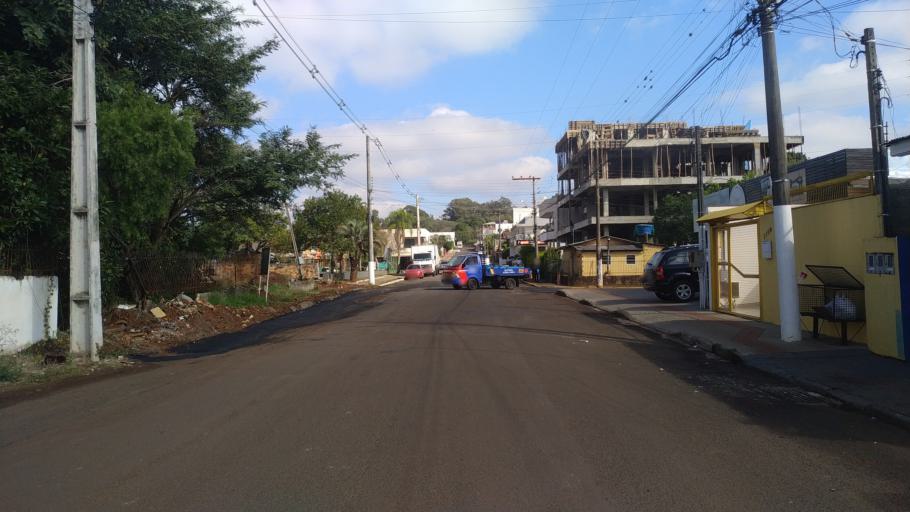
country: BR
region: Santa Catarina
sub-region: Chapeco
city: Chapeco
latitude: -27.0823
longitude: -52.6115
